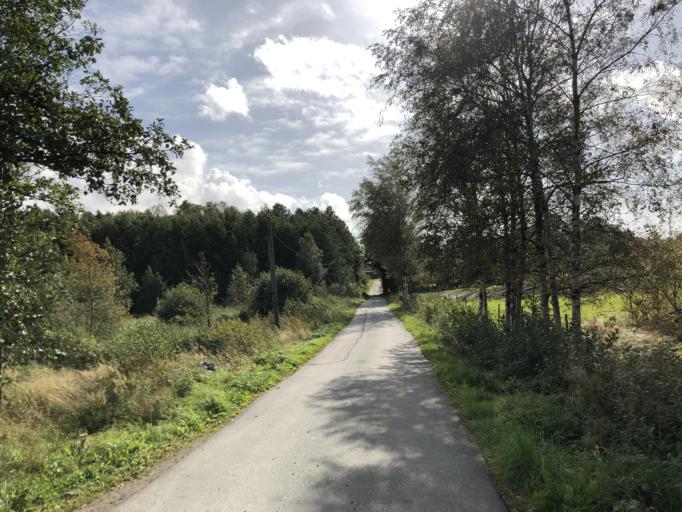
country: SE
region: Vaestra Goetaland
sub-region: Goteborg
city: Majorna
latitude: 57.7509
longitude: 11.8621
